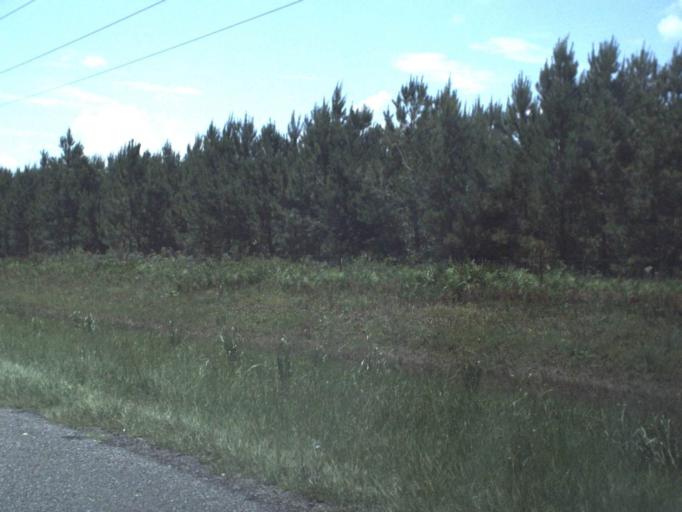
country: US
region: Florida
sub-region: Bradford County
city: Starke
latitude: 29.9709
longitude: -82.2091
